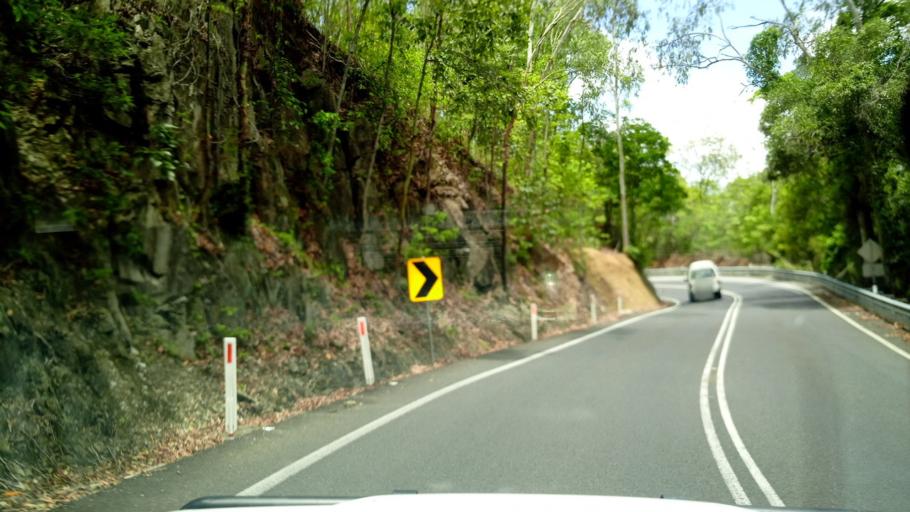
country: AU
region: Queensland
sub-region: Cairns
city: Redlynch
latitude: -16.8390
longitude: 145.6836
